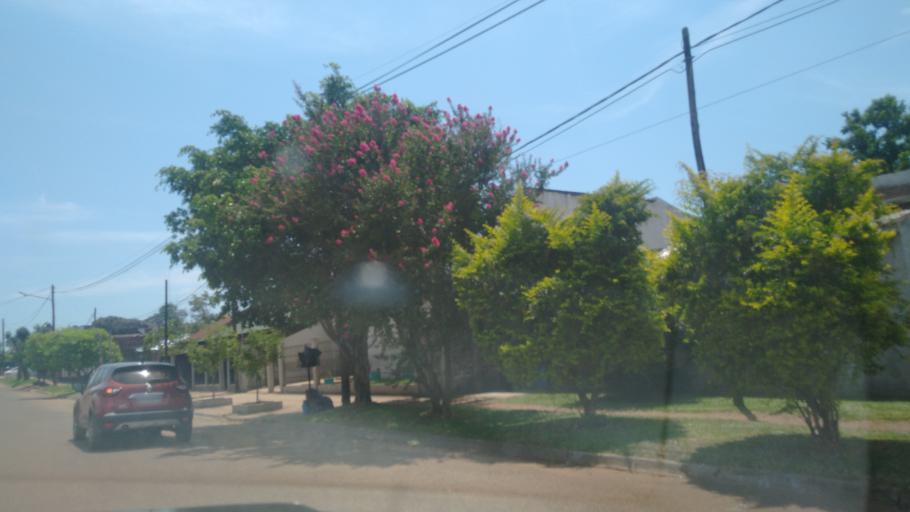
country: AR
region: Corrientes
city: Santo Tome
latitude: -28.5520
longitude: -56.0385
